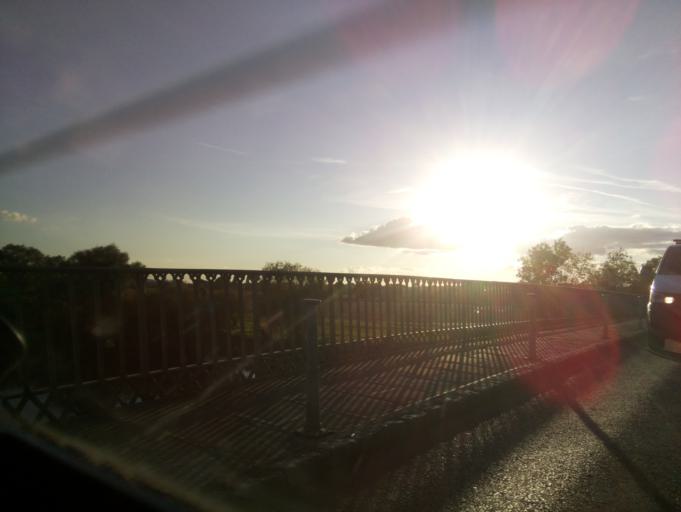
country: GB
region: England
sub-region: Gloucestershire
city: Tewkesbury
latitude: 52.0020
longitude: -2.1633
